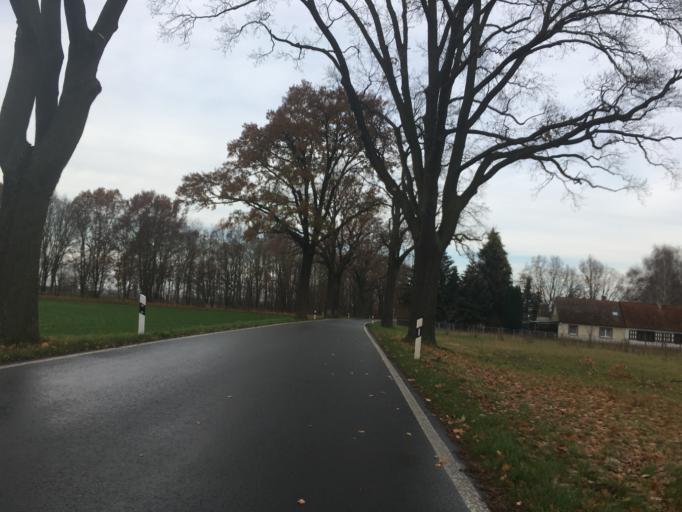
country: DE
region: Brandenburg
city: Letschin
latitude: 52.7014
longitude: 14.3998
